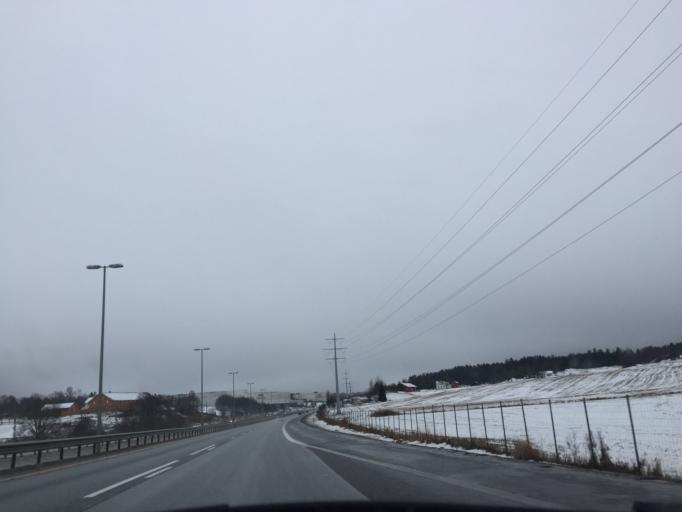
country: NO
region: Akershus
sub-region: Vestby
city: Vestby
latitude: 59.6000
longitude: 10.7385
